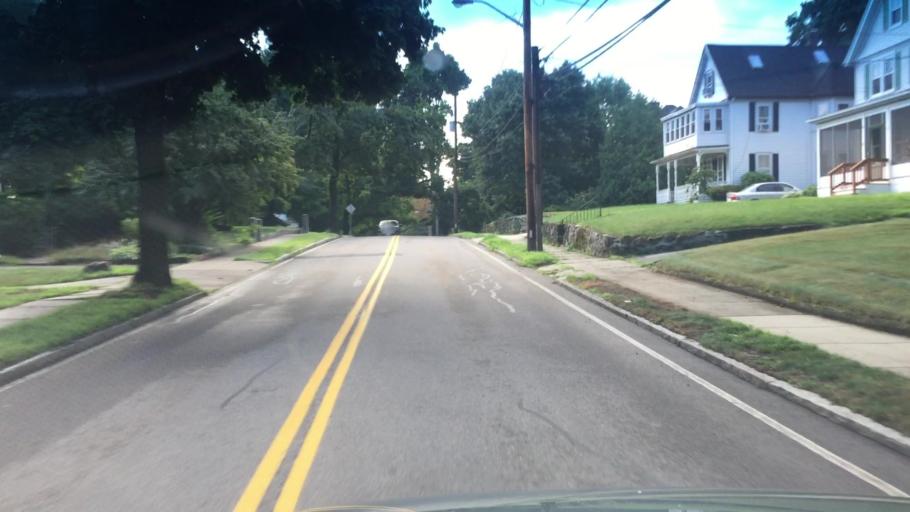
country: US
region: Massachusetts
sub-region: Norfolk County
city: Norwood
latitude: 42.1618
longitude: -71.2122
